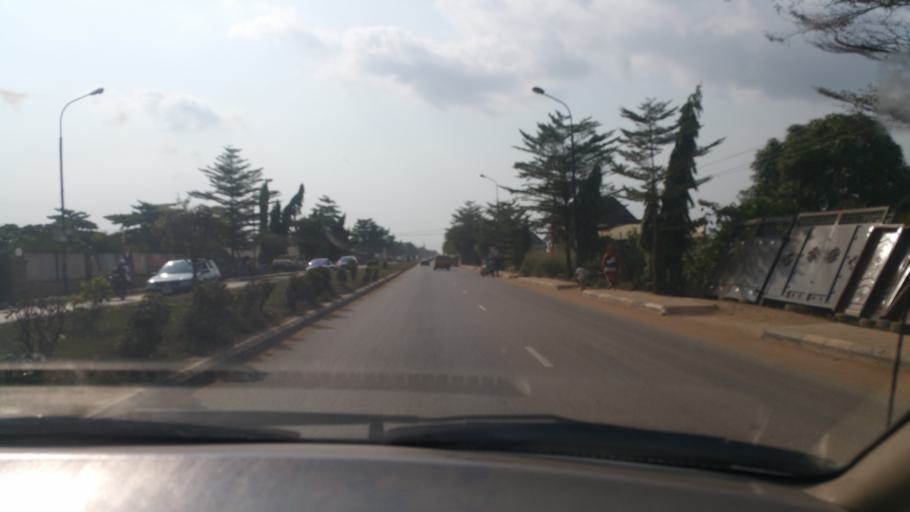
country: NG
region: Lagos
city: Ikotun
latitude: 6.5771
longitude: 3.2751
